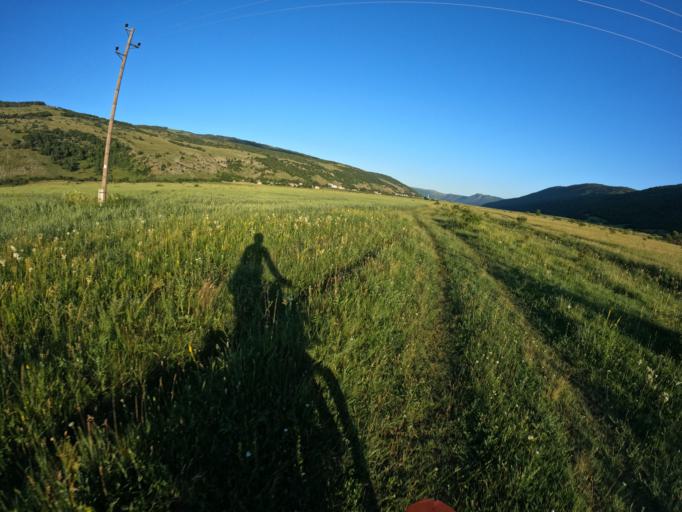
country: BA
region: Federation of Bosnia and Herzegovina
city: Glamoc
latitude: 43.9653
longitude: 16.9340
